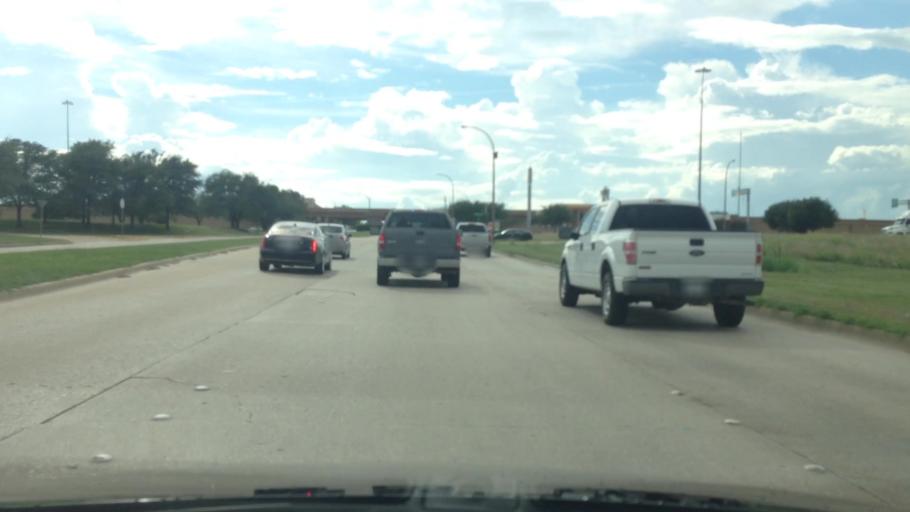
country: US
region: Texas
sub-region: Tarrant County
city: Haltom City
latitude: 32.8236
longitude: -97.3075
